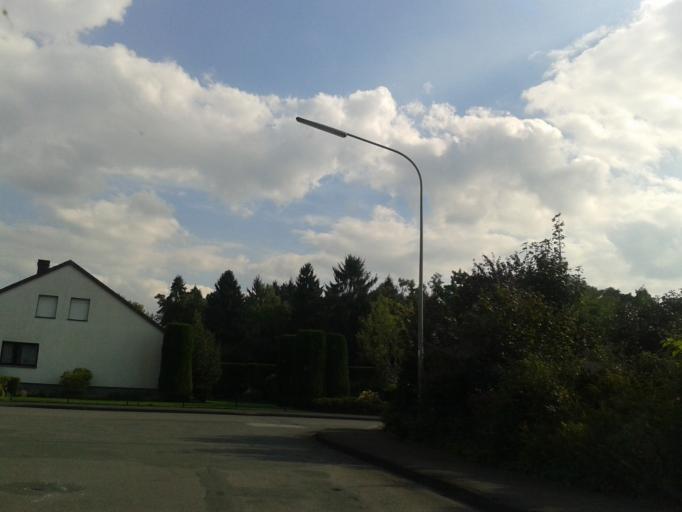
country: DE
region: North Rhine-Westphalia
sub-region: Regierungsbezirk Detmold
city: Schlangen
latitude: 51.8003
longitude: 8.8325
